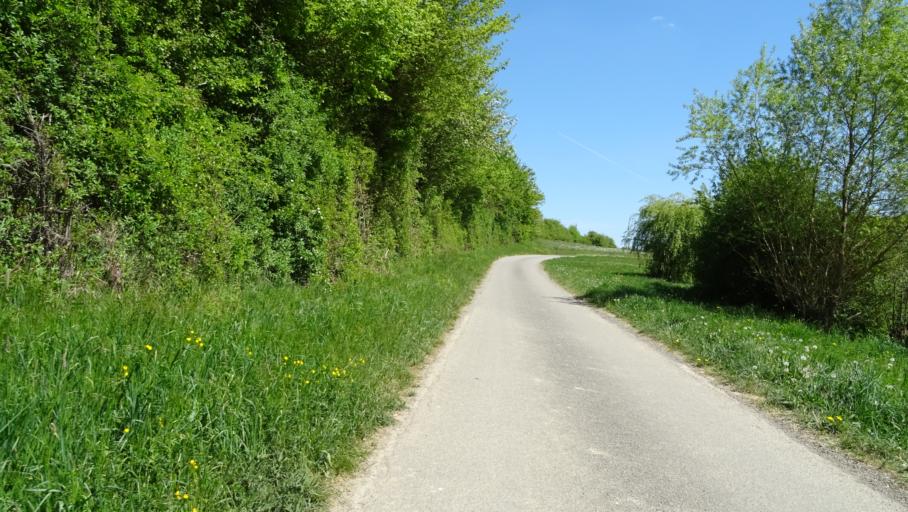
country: DE
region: Baden-Wuerttemberg
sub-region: Karlsruhe Region
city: Limbach
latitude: 49.4140
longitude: 9.2404
